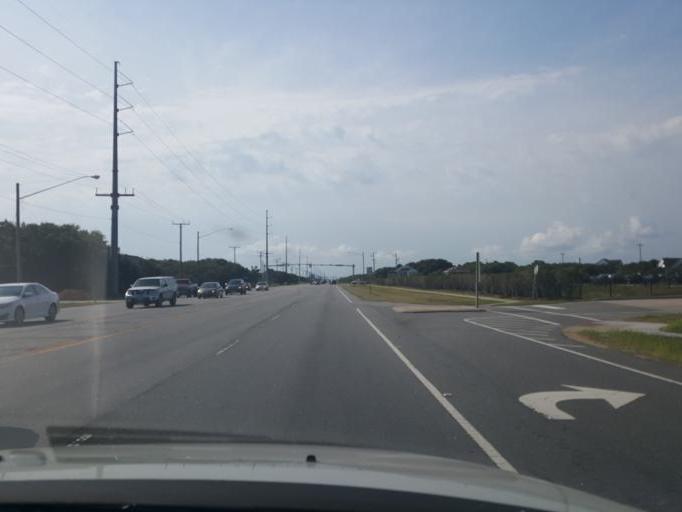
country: US
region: North Carolina
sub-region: Dare County
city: Kill Devil Hills
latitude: 36.0279
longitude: -75.6696
